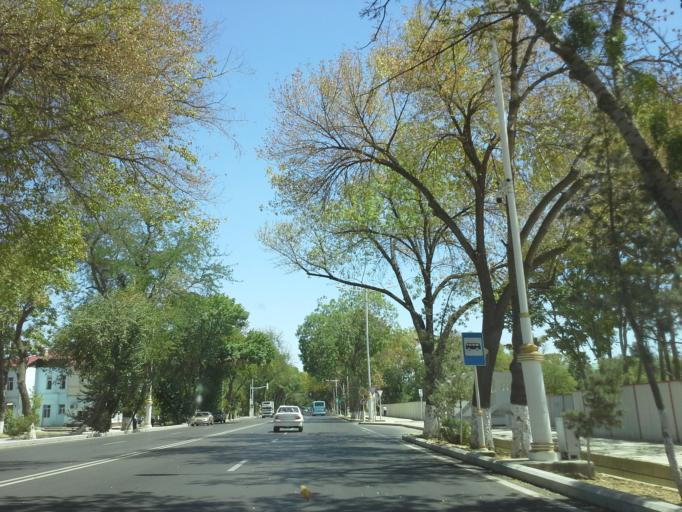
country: TM
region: Ahal
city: Ashgabat
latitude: 37.9341
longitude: 58.4030
